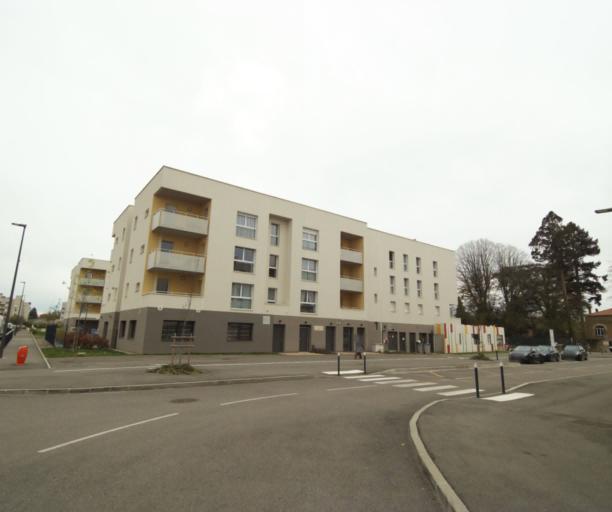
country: FR
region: Bourgogne
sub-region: Departement de Saone-et-Loire
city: Charnay-les-Macon
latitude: 46.3104
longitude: 4.8060
